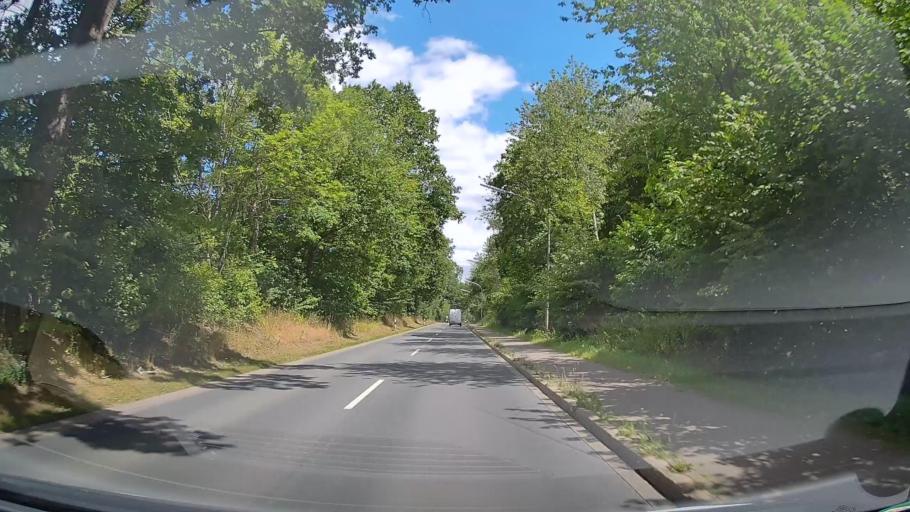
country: DE
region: Lower Saxony
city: Osnabrueck
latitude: 52.3100
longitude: 8.0807
